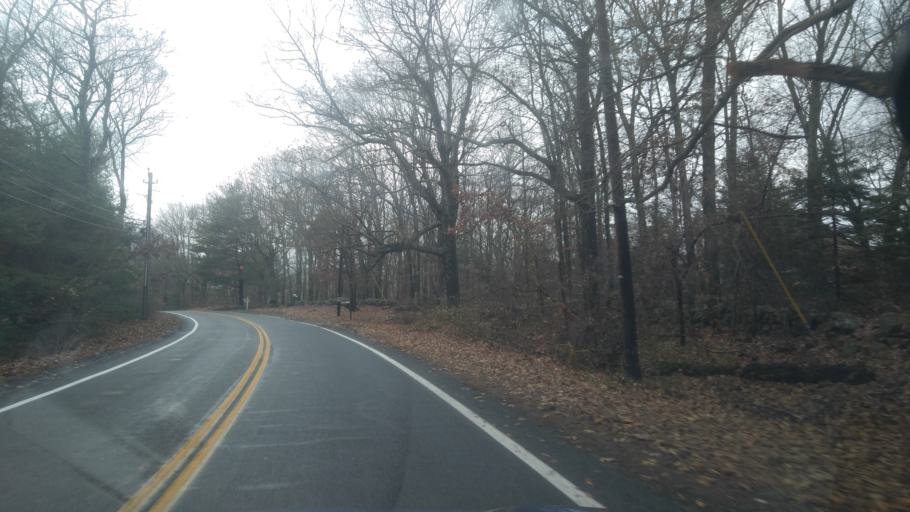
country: US
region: Rhode Island
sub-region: Kent County
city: West Warwick
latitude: 41.6615
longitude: -71.5196
